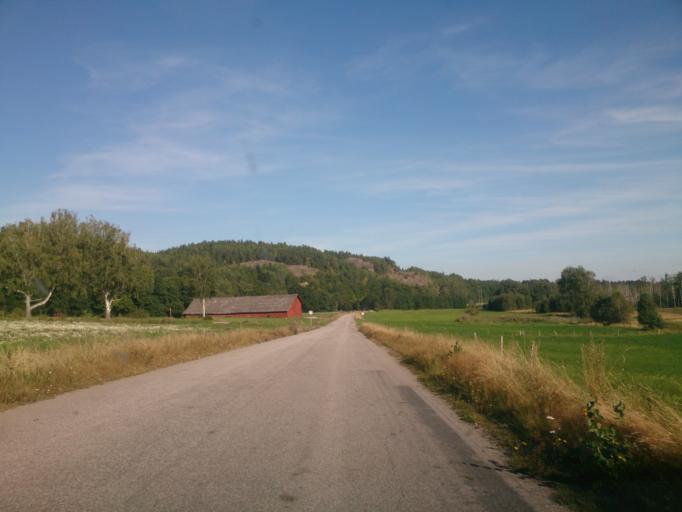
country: SE
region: OEstergoetland
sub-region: Norrkopings Kommun
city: Jursla
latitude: 58.6733
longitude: 16.1463
